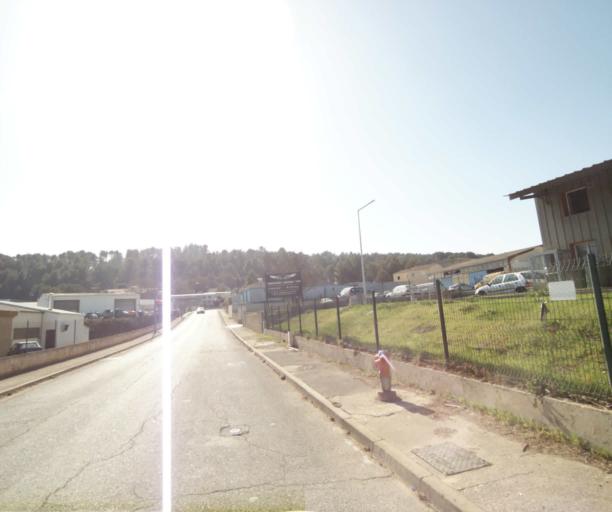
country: FR
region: Provence-Alpes-Cote d'Azur
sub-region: Departement des Bouches-du-Rhone
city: Gardanne
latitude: 43.4465
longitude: 5.4547
